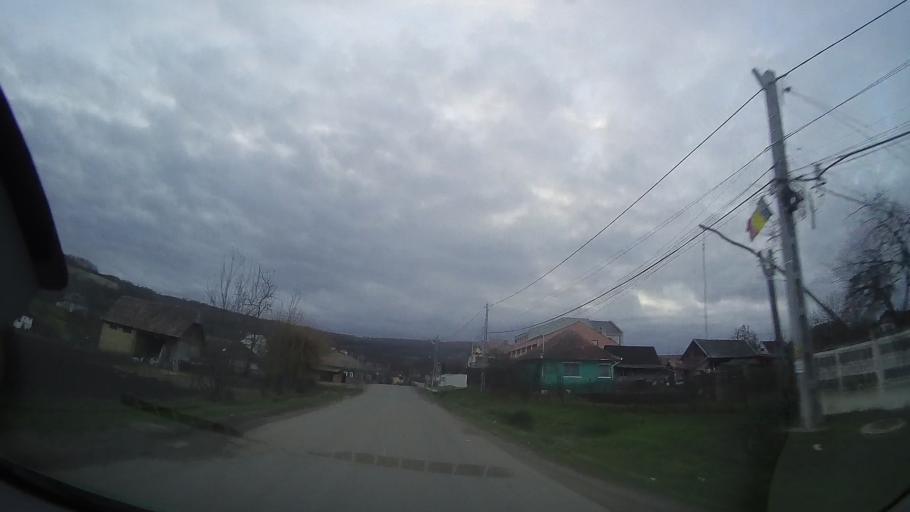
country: RO
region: Cluj
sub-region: Comuna Palatca
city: Palatca
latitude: 46.8404
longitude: 23.9876
